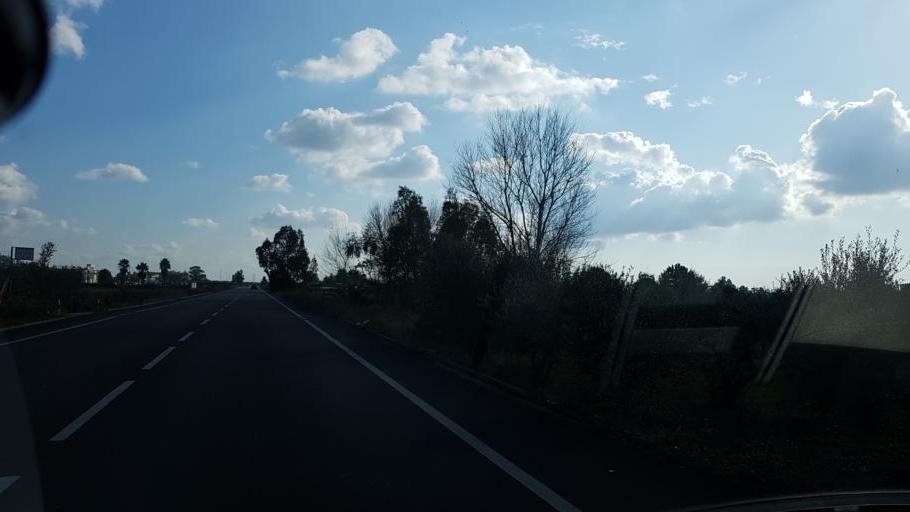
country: IT
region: Apulia
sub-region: Provincia di Lecce
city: Veglie
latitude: 40.3442
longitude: 17.9765
